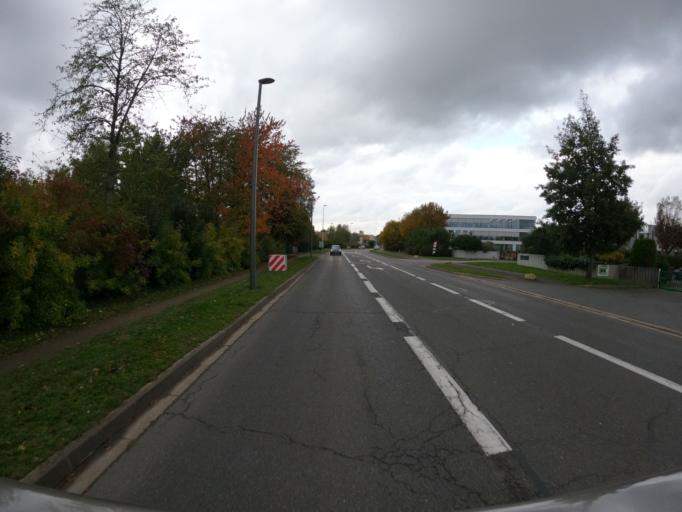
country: FR
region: Ile-de-France
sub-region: Departement de Seine-et-Marne
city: Emerainville
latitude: 48.8159
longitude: 2.6190
